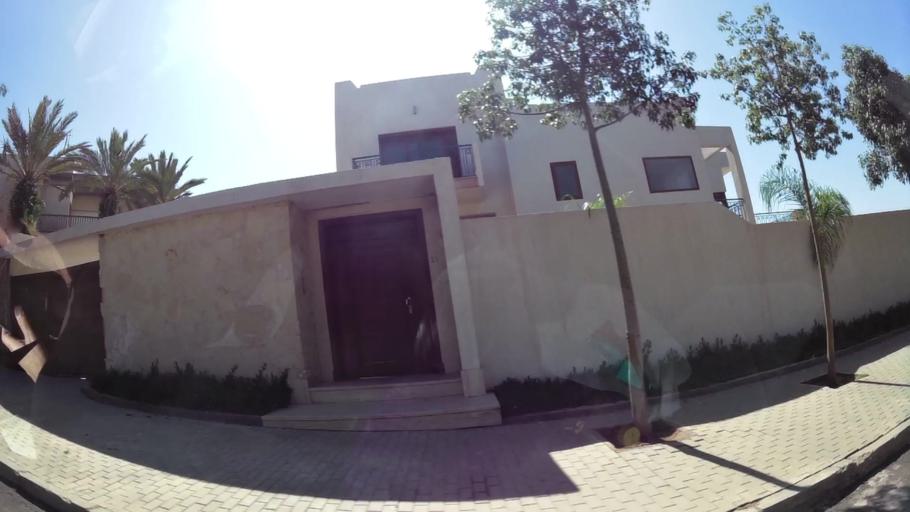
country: MA
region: Souss-Massa-Draa
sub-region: Agadir-Ida-ou-Tnan
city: Agadir
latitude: 30.4416
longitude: -9.5816
